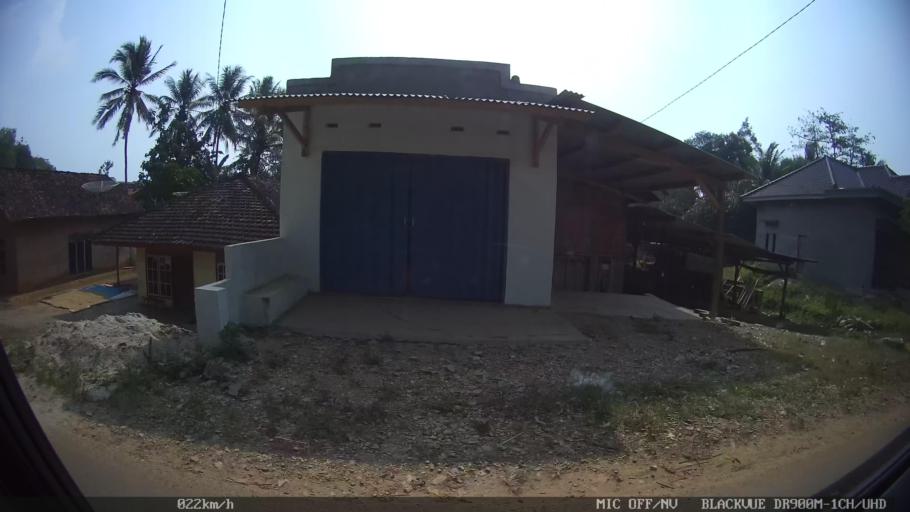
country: ID
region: Lampung
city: Pringsewu
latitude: -5.3963
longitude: 104.9921
